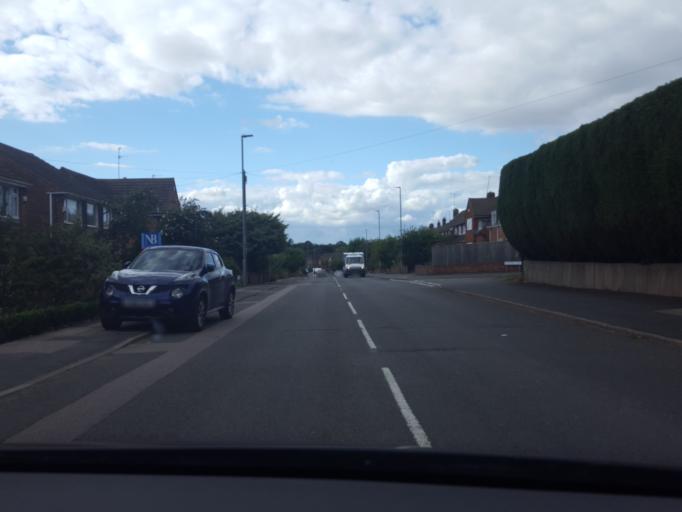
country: GB
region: England
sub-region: Leicestershire
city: Loughborough
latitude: 52.7545
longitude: -1.2239
